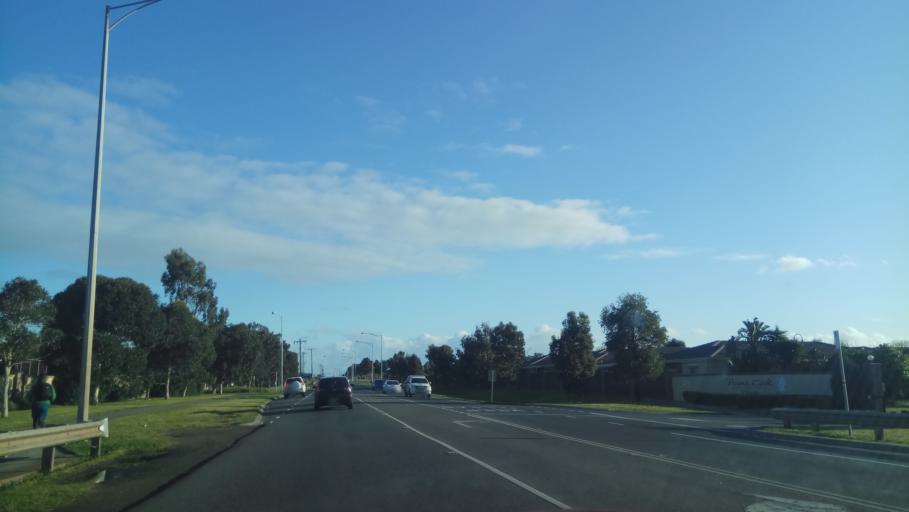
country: AU
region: Victoria
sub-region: Wyndham
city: Point Cook
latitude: -37.8980
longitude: 144.7540
